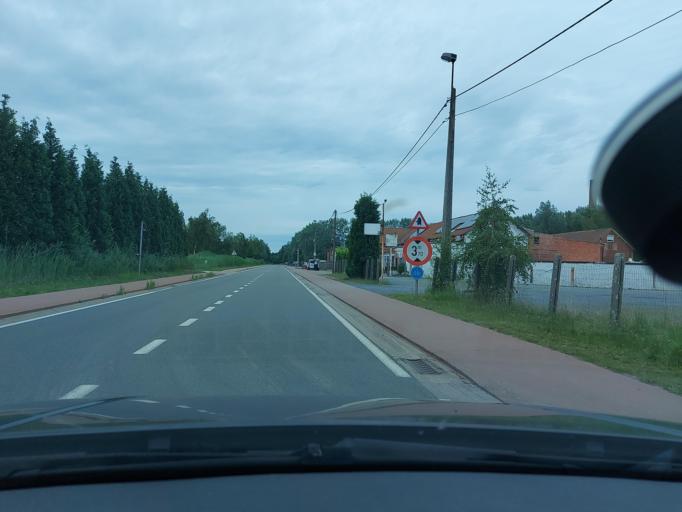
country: BE
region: Flanders
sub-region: Provincie Antwerpen
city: Balen
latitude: 51.1974
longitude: 5.2267
